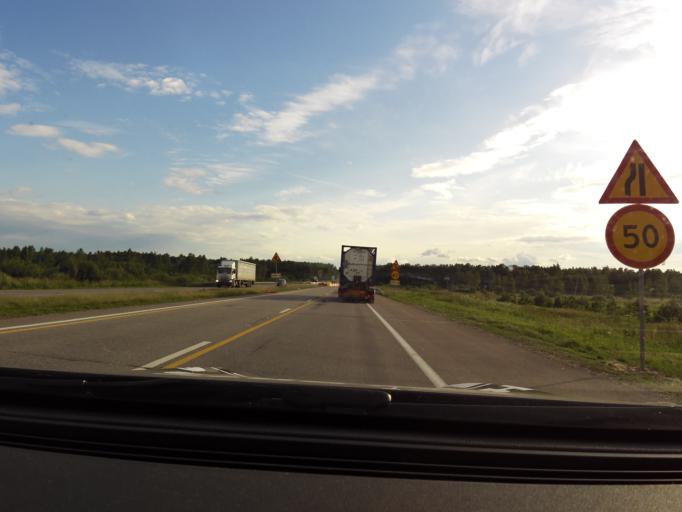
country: RU
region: Vladimir
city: Sudogda
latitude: 56.1269
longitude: 40.8695
